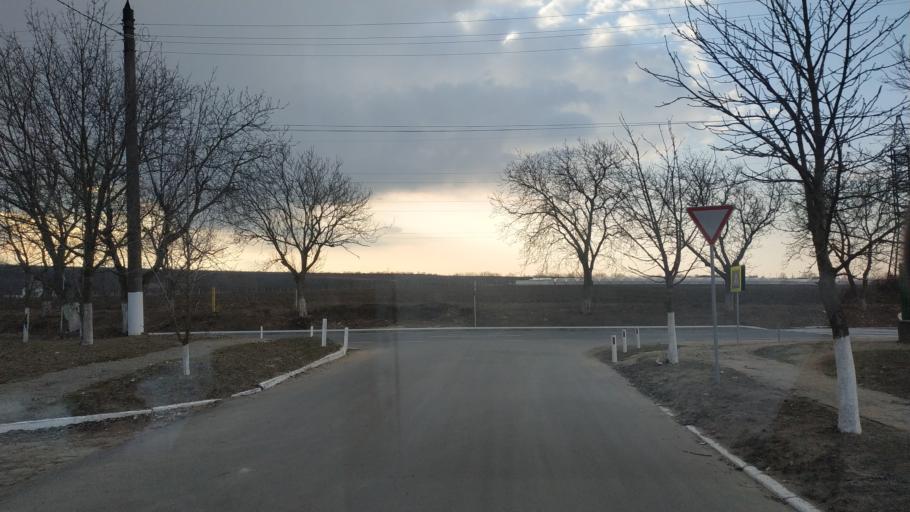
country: MD
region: Telenesti
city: Grigoriopol
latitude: 47.0126
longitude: 29.2891
